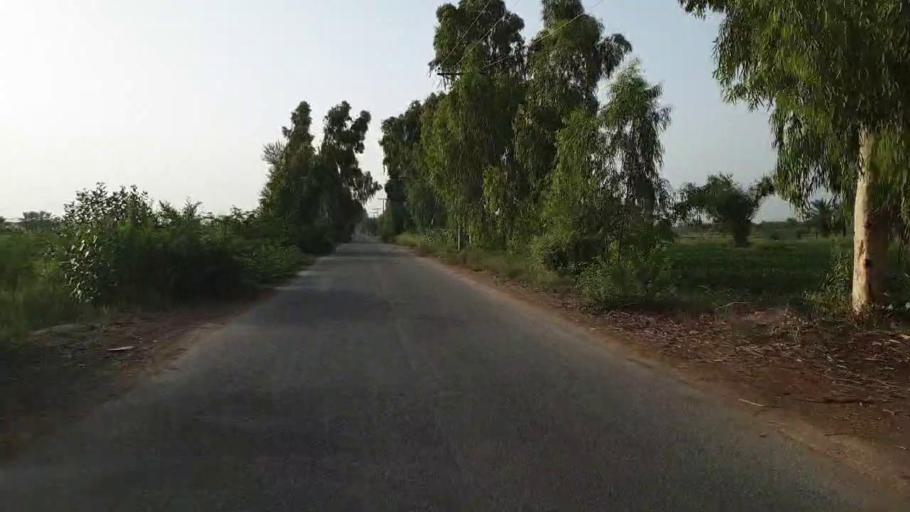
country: PK
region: Sindh
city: Bozdar
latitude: 27.1086
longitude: 68.9604
